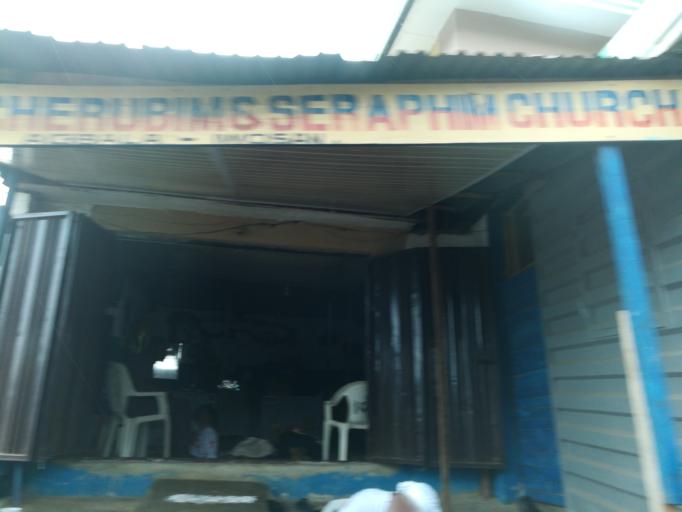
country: NG
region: Lagos
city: Oshodi
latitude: 6.5583
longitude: 3.3397
